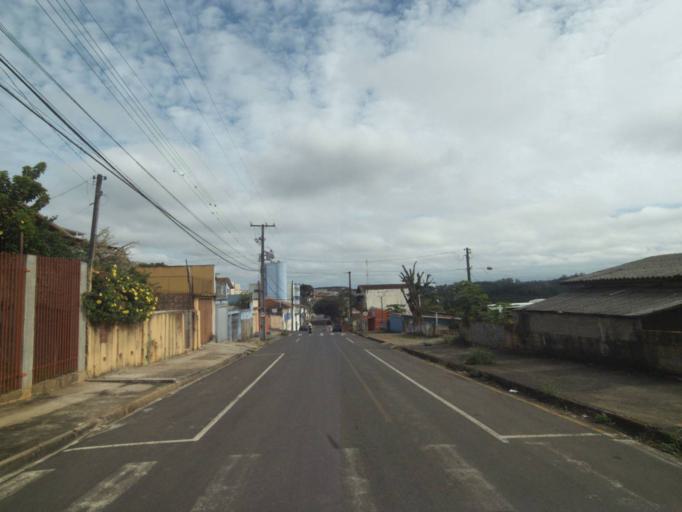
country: BR
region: Parana
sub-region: Telemaco Borba
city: Telemaco Borba
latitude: -24.3225
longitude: -50.6170
